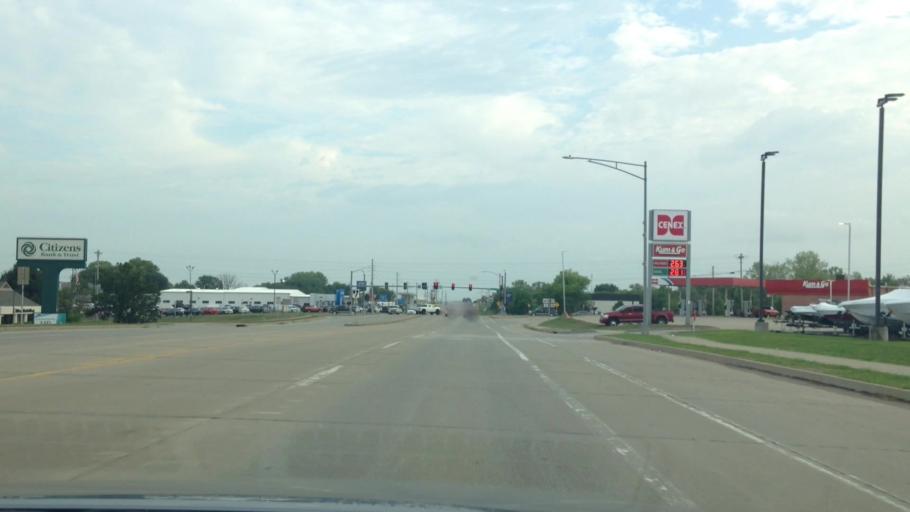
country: US
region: Missouri
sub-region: Clay County
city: Smithville
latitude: 39.3706
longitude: -94.5833
